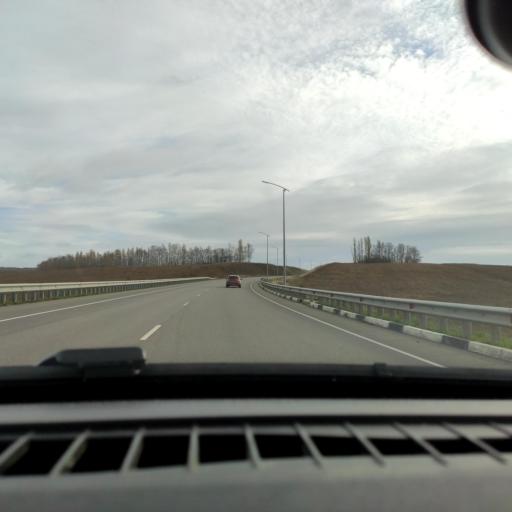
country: RU
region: Belgorod
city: Ilovka
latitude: 50.6732
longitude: 38.6113
